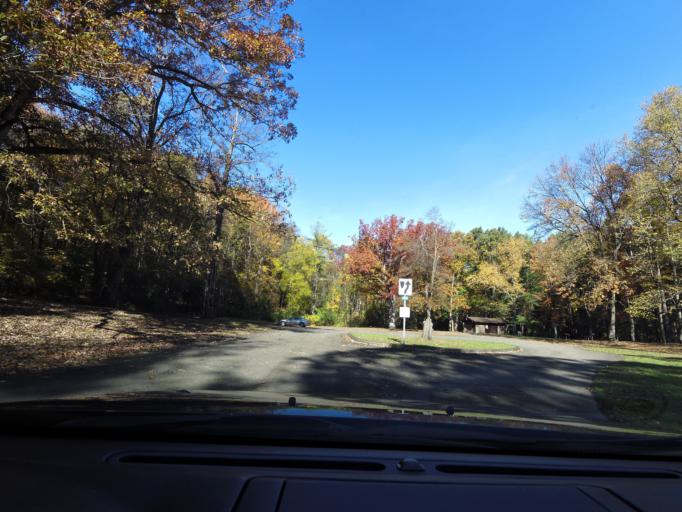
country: US
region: New York
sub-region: Wyoming County
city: Castile
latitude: 42.6180
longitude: -77.9959
